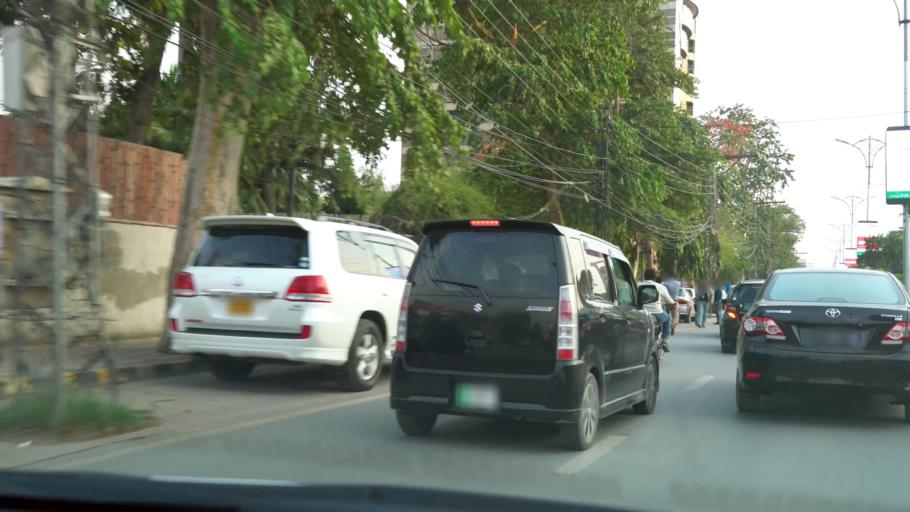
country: PK
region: Punjab
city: Lahore
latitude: 31.5130
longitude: 74.3512
